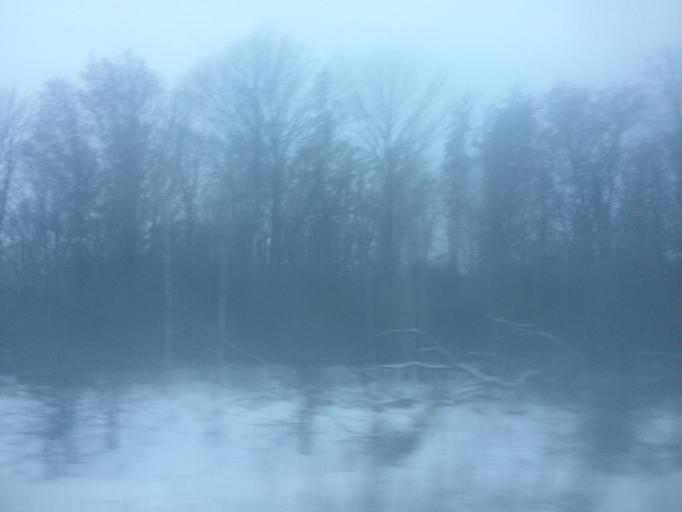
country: RU
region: Tula
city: Bogoroditsk
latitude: 53.8041
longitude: 38.1274
